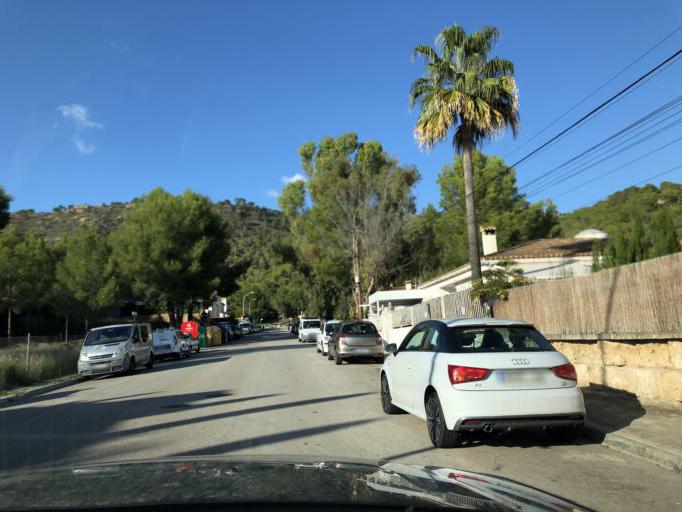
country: ES
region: Balearic Islands
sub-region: Illes Balears
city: Camp de Mar
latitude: 39.5387
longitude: 2.4393
